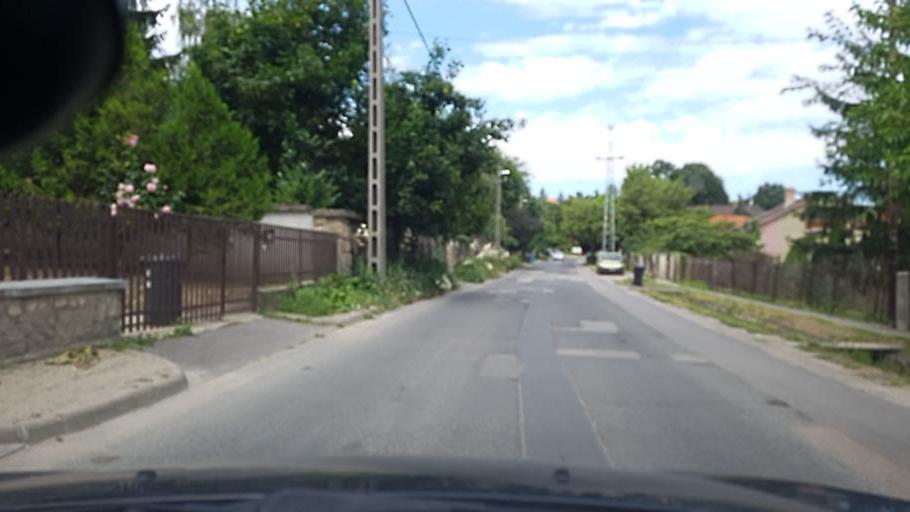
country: HU
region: Pest
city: Erd
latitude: 47.3976
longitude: 18.9287
